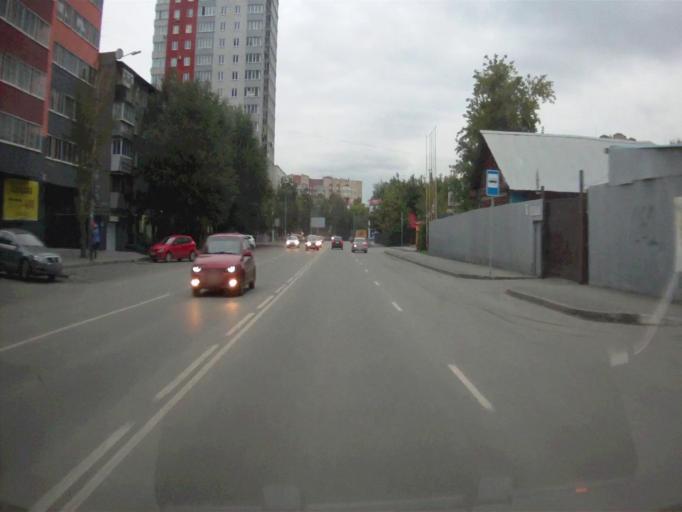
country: RU
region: Chelyabinsk
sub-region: Gorod Chelyabinsk
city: Chelyabinsk
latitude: 55.1516
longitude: 61.3985
